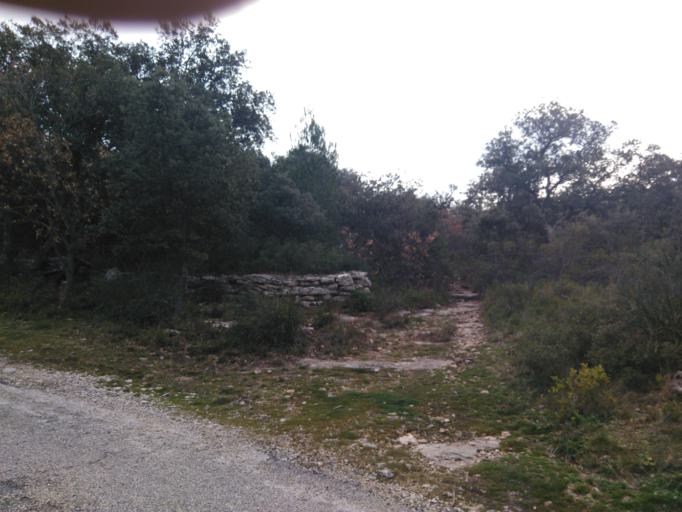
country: FR
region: Provence-Alpes-Cote d'Azur
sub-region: Departement du Vaucluse
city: Lagnes
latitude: 43.9425
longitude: 5.1182
